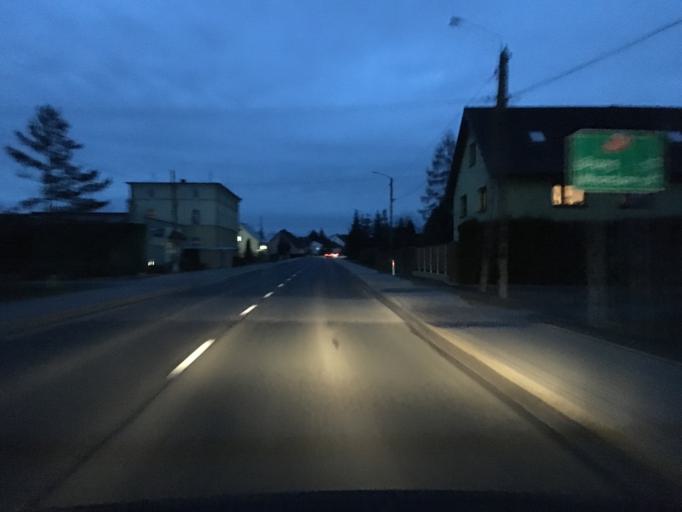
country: PL
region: Opole Voivodeship
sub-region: Powiat brzeski
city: Losiow
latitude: 50.7906
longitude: 17.5642
